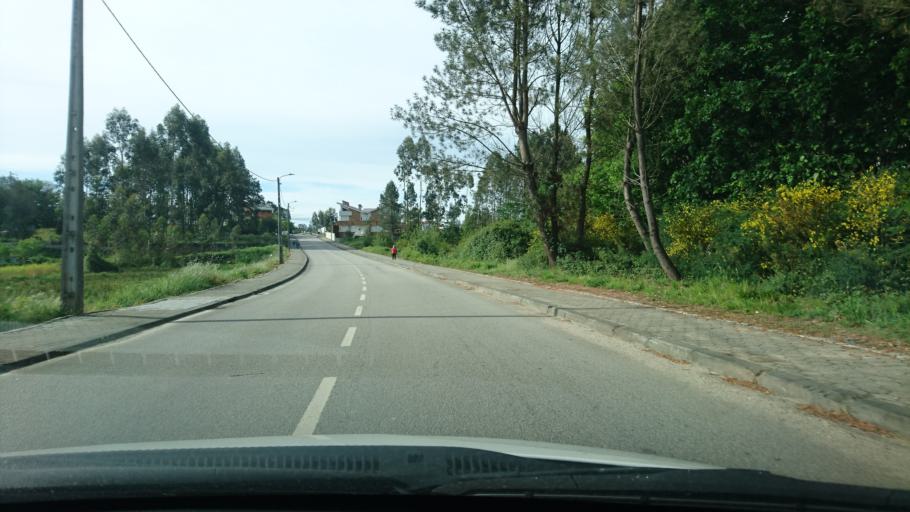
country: PT
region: Aveiro
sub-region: Oliveira de Azemeis
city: Sao Roque
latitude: 40.8740
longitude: -8.4762
